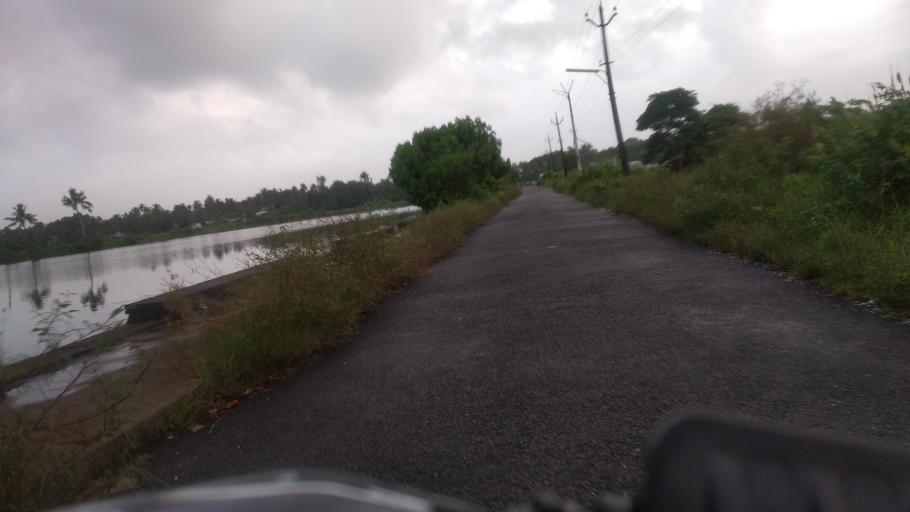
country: IN
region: Kerala
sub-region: Ernakulam
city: Elur
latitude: 10.0169
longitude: 76.2210
